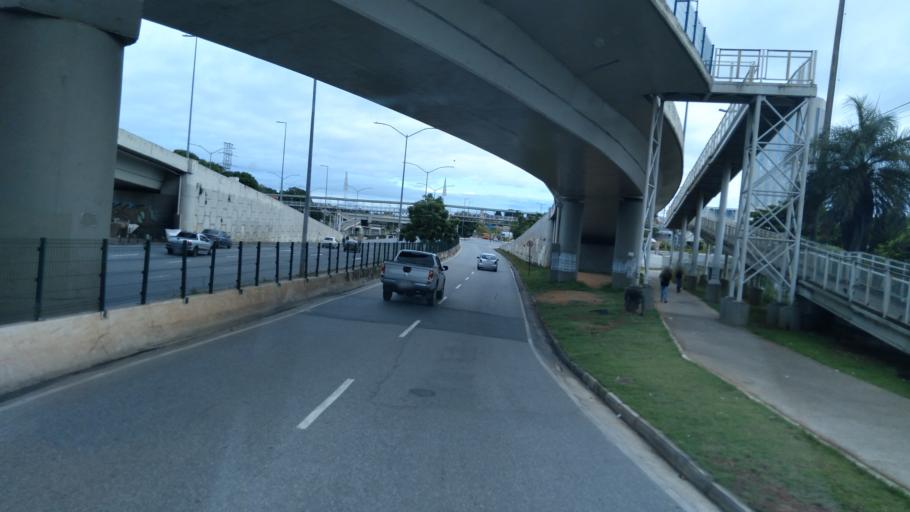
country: BR
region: Minas Gerais
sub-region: Belo Horizonte
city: Belo Horizonte
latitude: -19.8756
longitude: -43.9281
